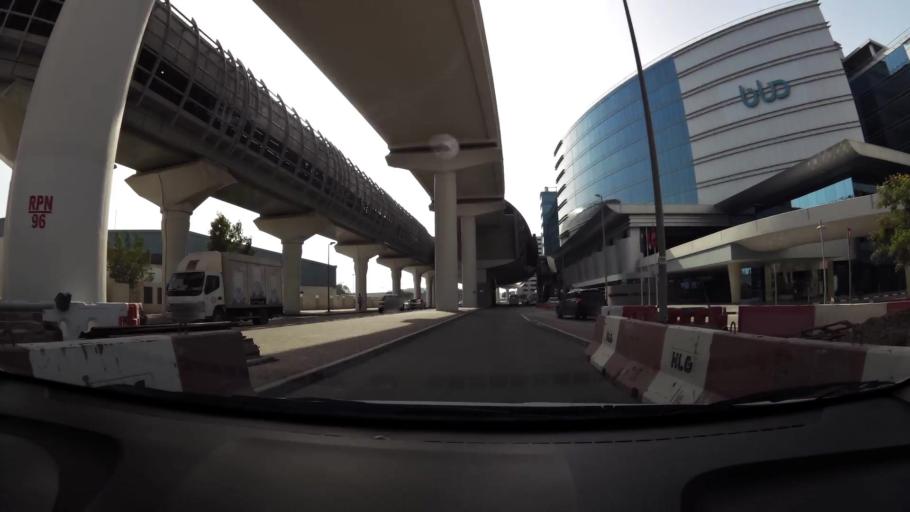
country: AE
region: Ash Shariqah
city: Sharjah
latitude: 25.2404
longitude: 55.3670
